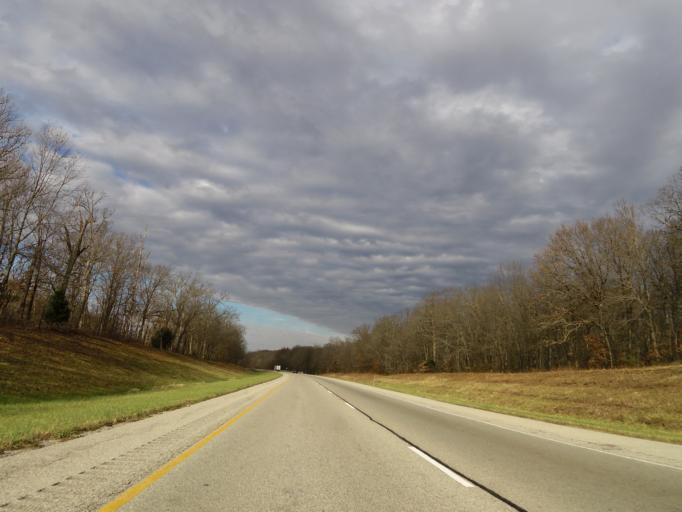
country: US
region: Illinois
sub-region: Washington County
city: Nashville
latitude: 38.3971
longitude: -89.3899
